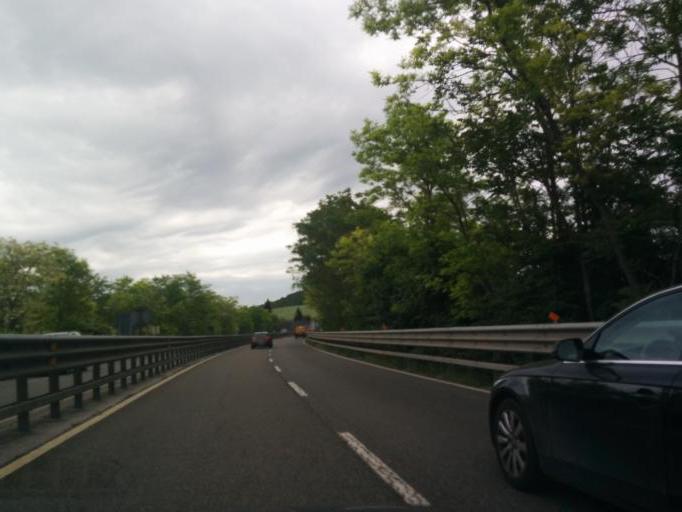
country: IT
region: Tuscany
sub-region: Provincia di Siena
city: Monteriggioni
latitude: 43.3893
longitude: 11.2677
